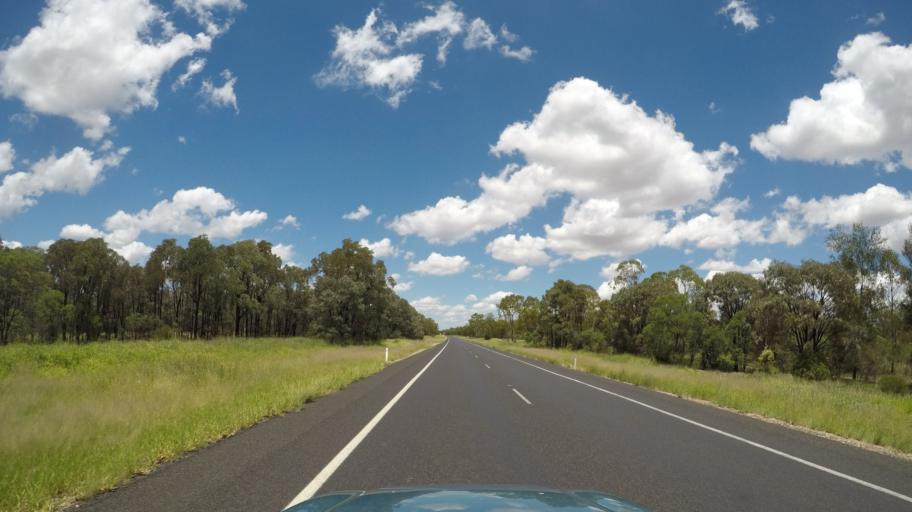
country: AU
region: Queensland
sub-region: Goondiwindi
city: Goondiwindi
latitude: -28.0730
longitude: 150.7486
